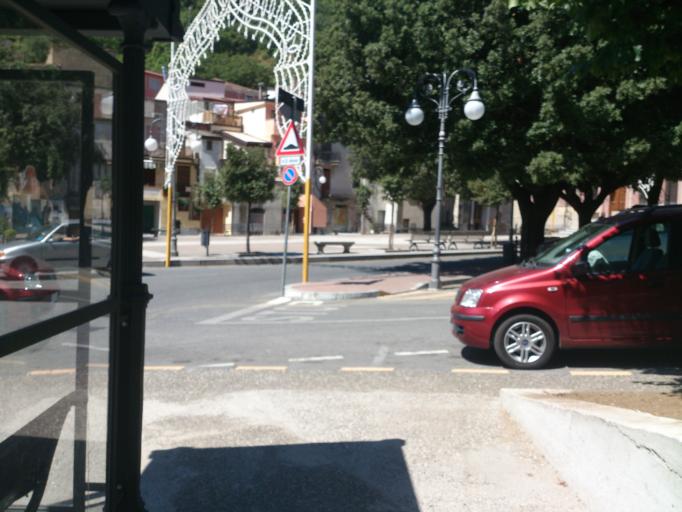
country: IT
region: Calabria
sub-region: Provincia di Reggio Calabria
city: Pazzano
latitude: 38.4755
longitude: 16.4530
